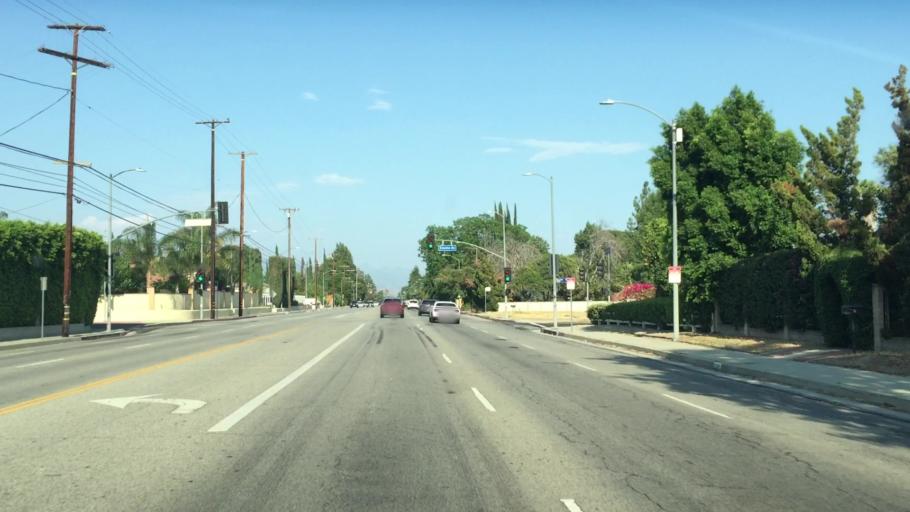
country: US
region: California
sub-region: Los Angeles County
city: Northridge
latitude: 34.2358
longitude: -118.5163
